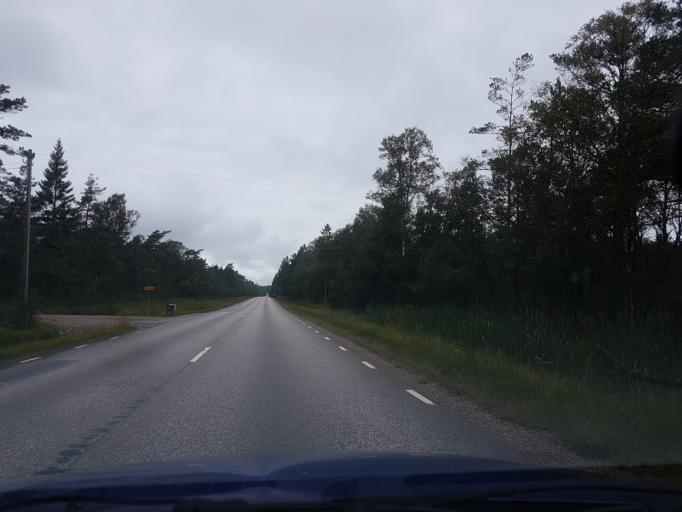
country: SE
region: Vaestra Goetaland
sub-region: Lerums Kommun
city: Grabo
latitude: 57.9211
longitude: 12.2958
